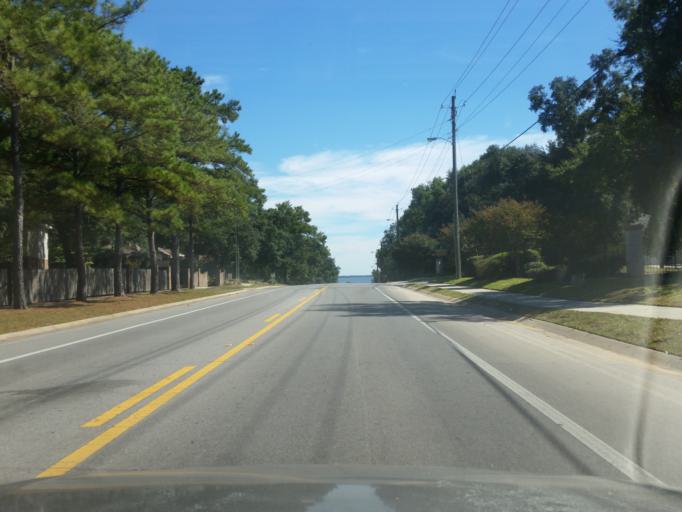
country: US
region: Florida
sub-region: Escambia County
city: Ferry Pass
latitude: 30.4823
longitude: -87.1679
